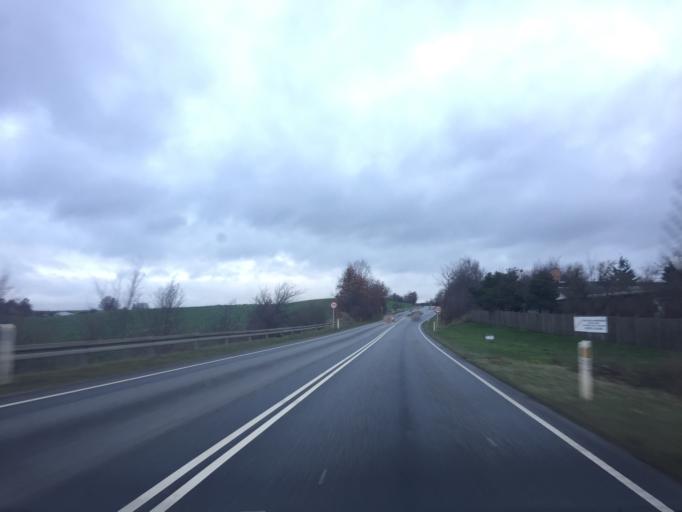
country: DK
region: Capital Region
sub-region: Frederikssund Kommune
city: Skibby
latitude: 55.7584
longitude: 11.9550
